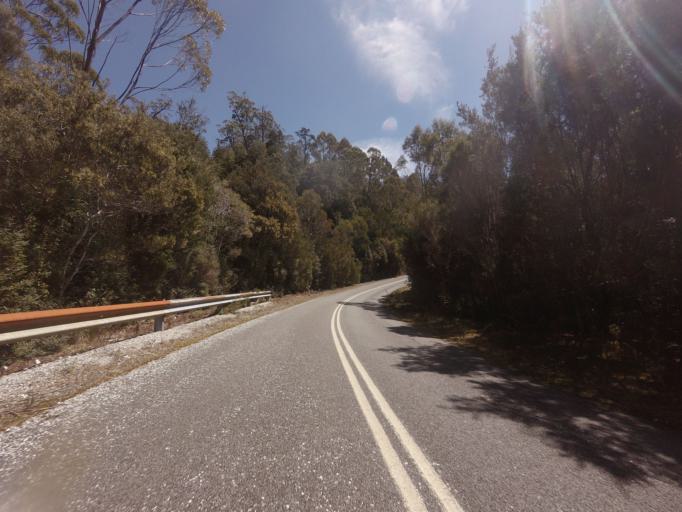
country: AU
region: Tasmania
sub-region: West Coast
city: Queenstown
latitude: -42.7689
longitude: 146.0070
